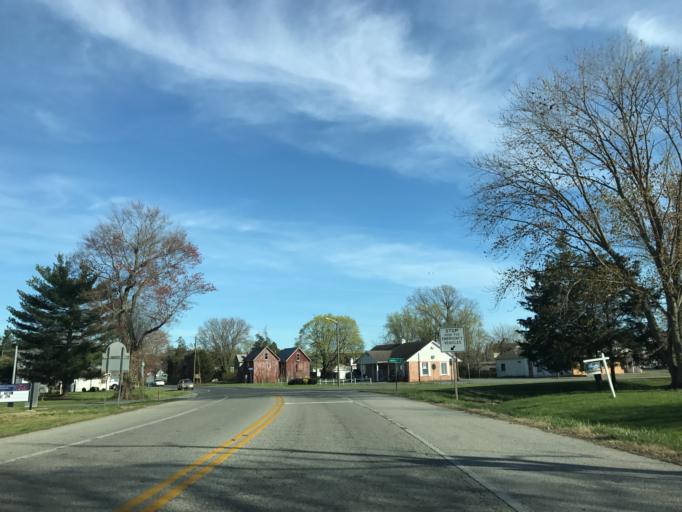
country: US
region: Maryland
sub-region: Caroline County
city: Greensboro
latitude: 39.1131
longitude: -75.7463
